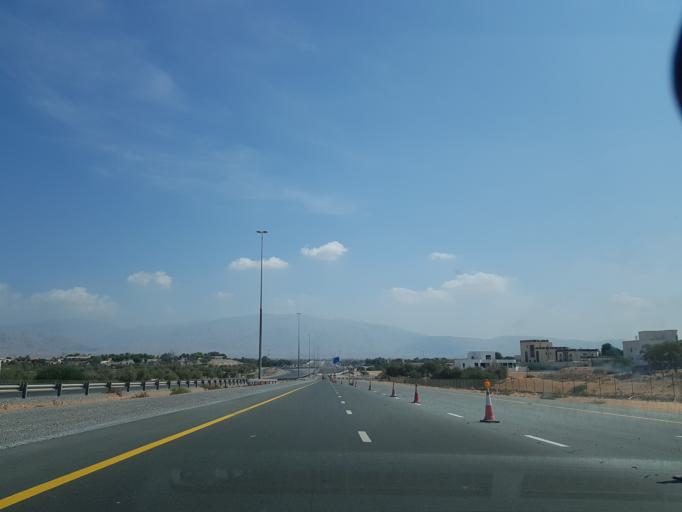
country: AE
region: Ra's al Khaymah
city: Ras al-Khaimah
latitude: 25.7032
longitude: 55.9562
